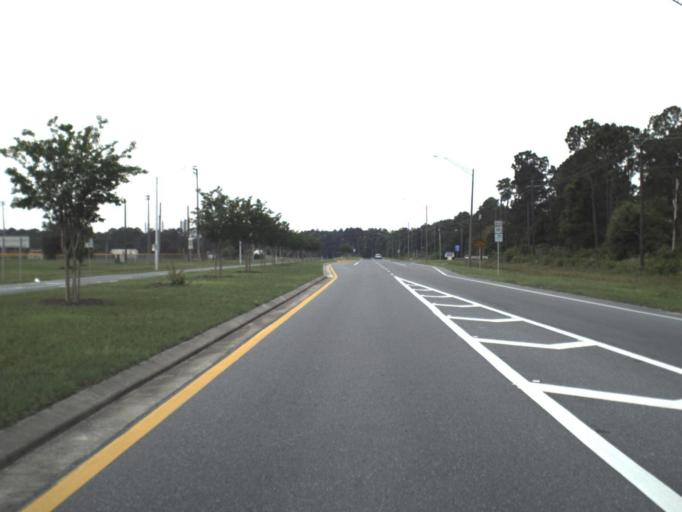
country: US
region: Florida
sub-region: Putnam County
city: Palatka
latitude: 29.6682
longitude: -81.6576
